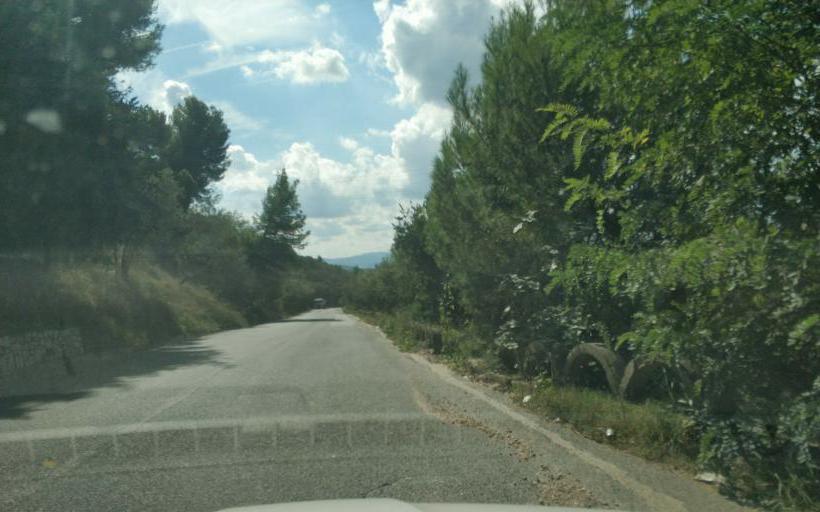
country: AL
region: Durres
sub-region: Rrethi i Krujes
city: Kruje
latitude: 41.4872
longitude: 19.7673
